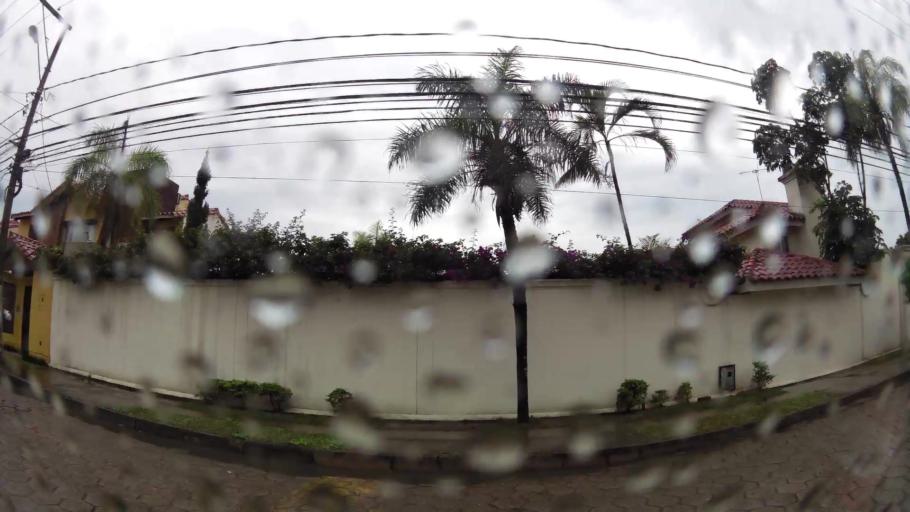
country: BO
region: Santa Cruz
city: Santa Cruz de la Sierra
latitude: -17.7994
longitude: -63.2128
